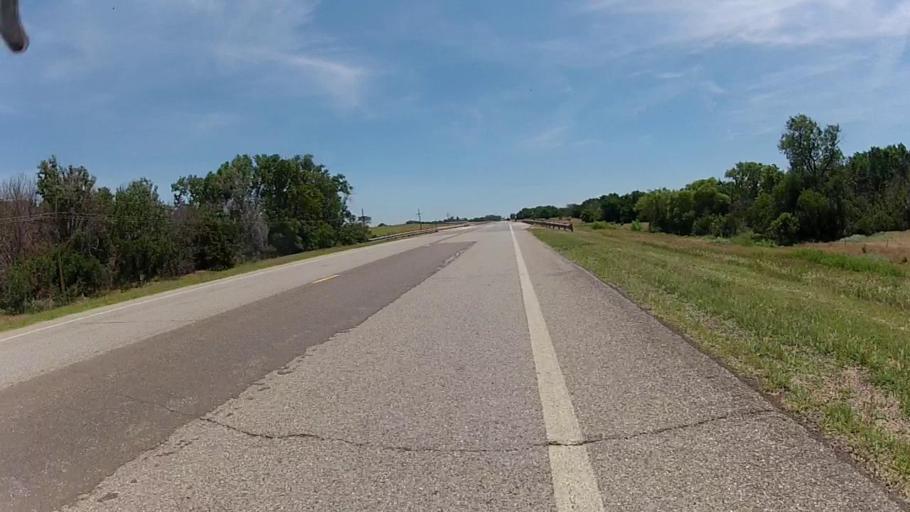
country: US
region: Kansas
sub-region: Barber County
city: Medicine Lodge
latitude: 37.2534
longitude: -98.4739
